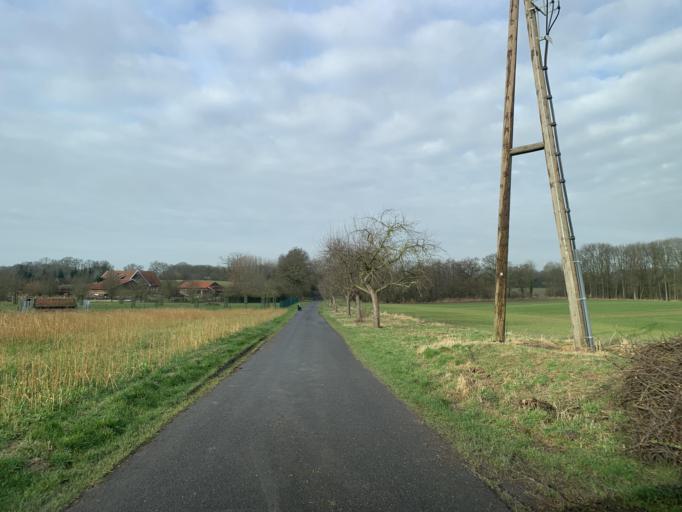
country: DE
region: North Rhine-Westphalia
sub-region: Regierungsbezirk Munster
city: Altenberge
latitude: 52.0484
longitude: 7.4526
